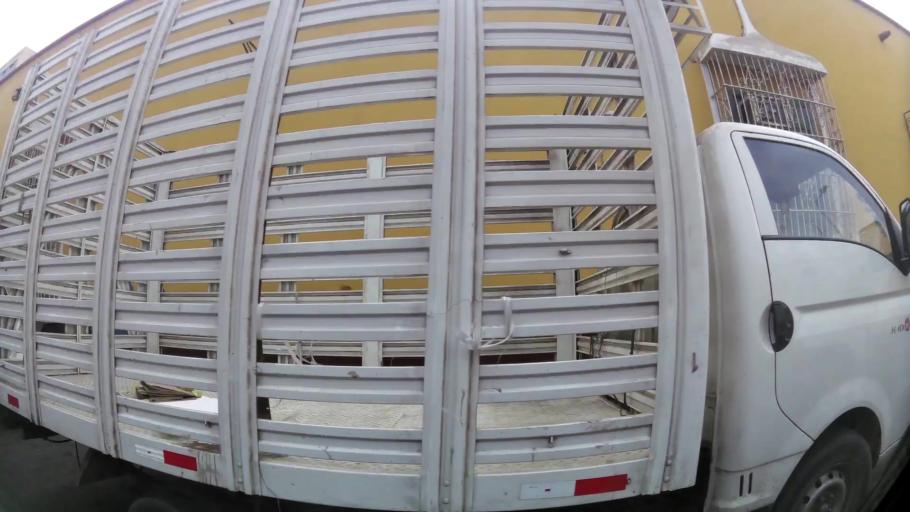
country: PE
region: La Libertad
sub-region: Provincia de Trujillo
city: Trujillo
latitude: -8.1111
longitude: -79.0242
